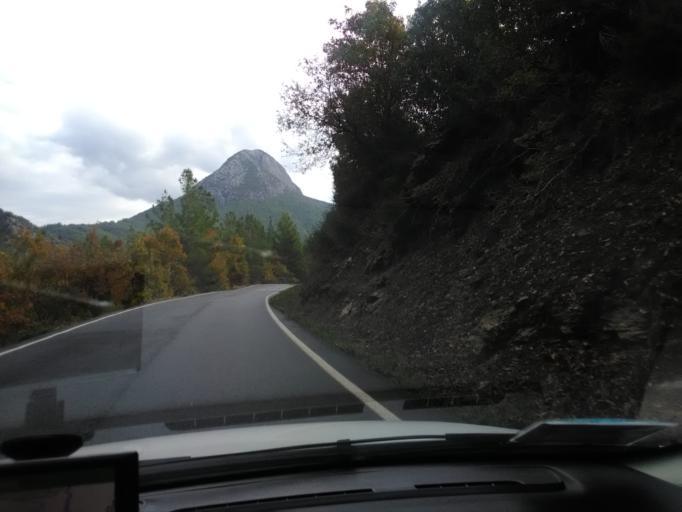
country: TR
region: Antalya
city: Gazipasa
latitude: 36.2504
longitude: 32.4052
